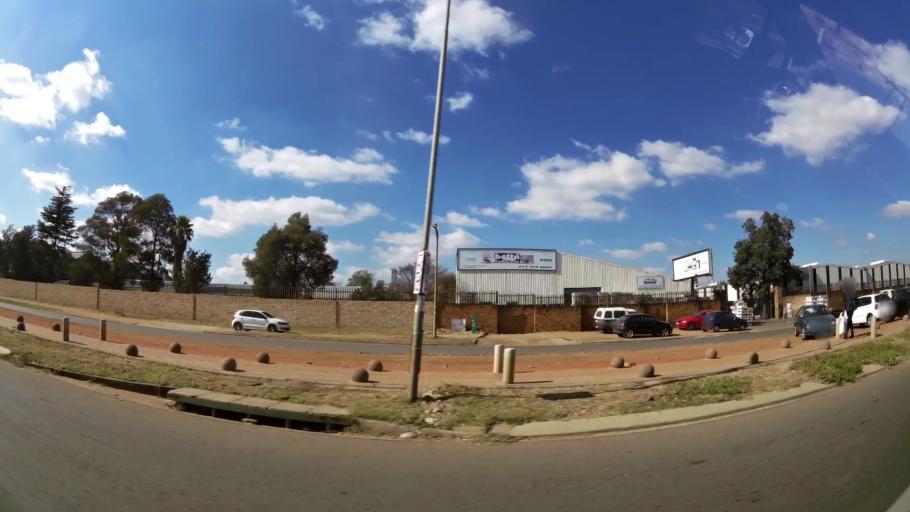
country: ZA
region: Gauteng
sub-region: West Rand District Municipality
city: Krugersdorp
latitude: -26.1476
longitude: 27.7896
